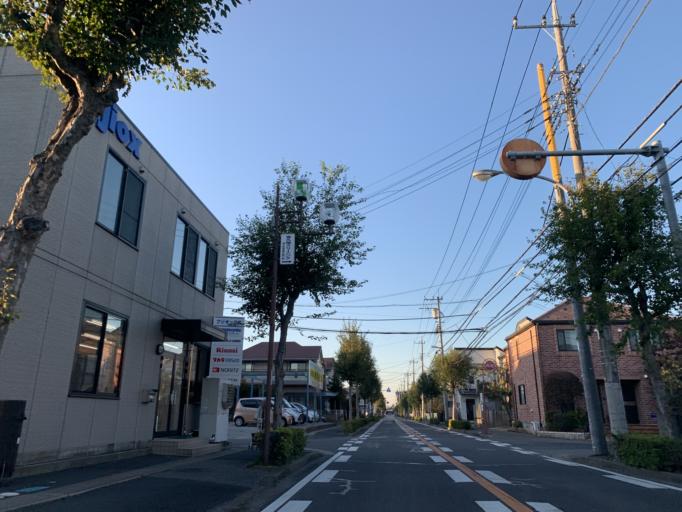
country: JP
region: Chiba
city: Nagareyama
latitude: 35.8889
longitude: 139.9180
